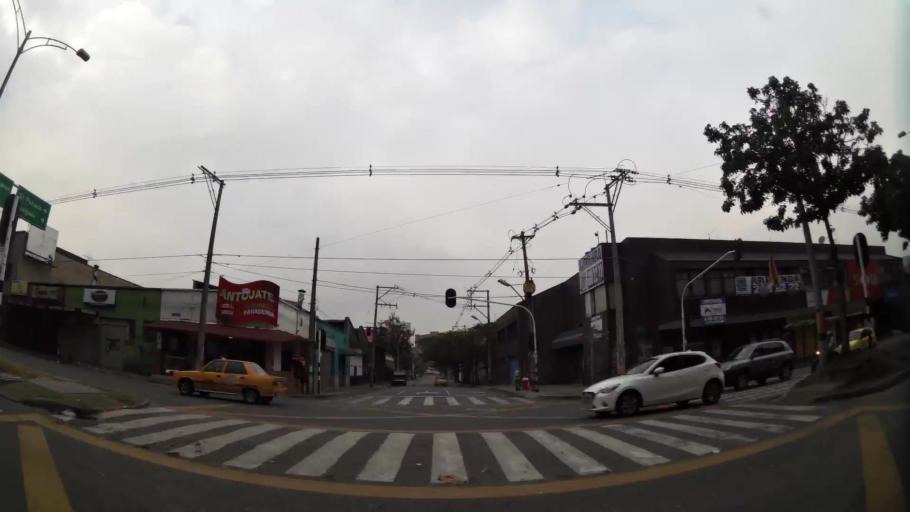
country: CO
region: Antioquia
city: Medellin
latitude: 6.2286
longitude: -75.5706
